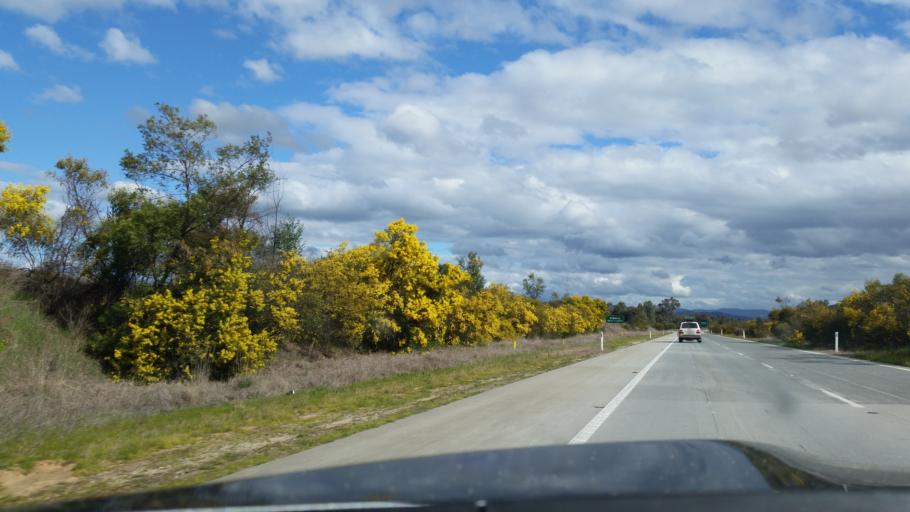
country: AU
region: New South Wales
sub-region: Albury Municipality
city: Lavington
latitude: -36.0135
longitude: 146.9869
